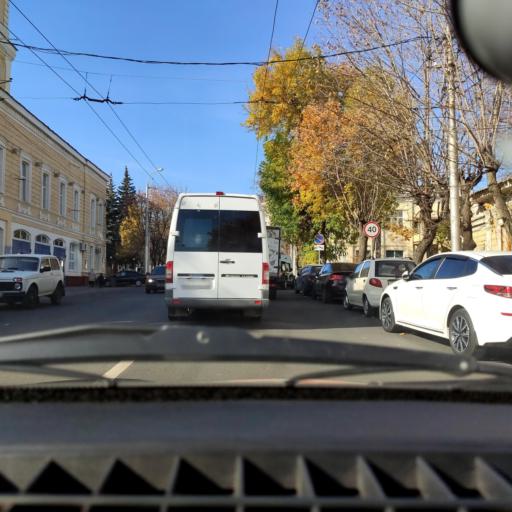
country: RU
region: Bashkortostan
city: Ufa
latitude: 54.7228
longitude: 55.9529
